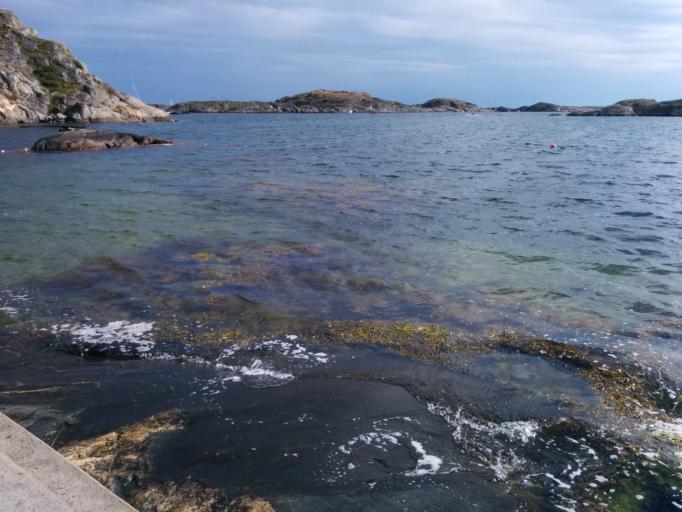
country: SE
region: Vaestra Goetaland
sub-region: Lysekils Kommun
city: Lysekil
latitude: 58.1205
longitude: 11.4436
